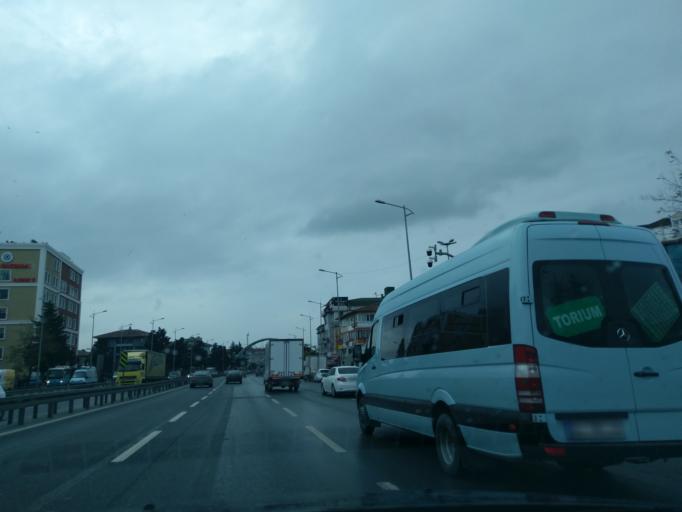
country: TR
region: Istanbul
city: Bueyuekcekmece
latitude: 41.0220
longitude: 28.5836
